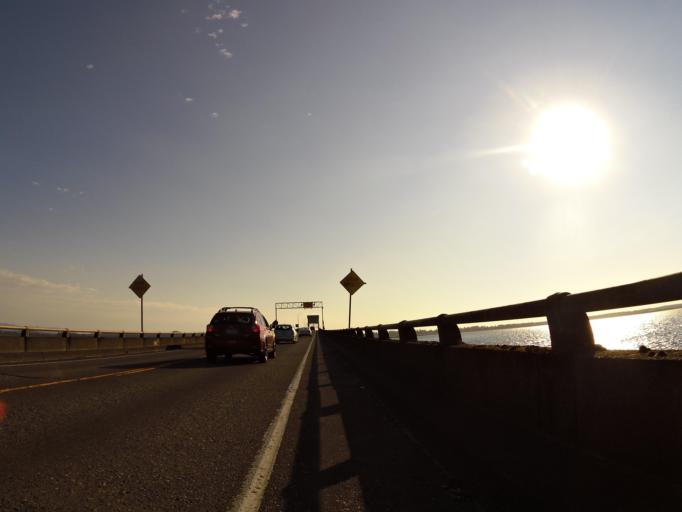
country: US
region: Oregon
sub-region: Clatsop County
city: Astoria
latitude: 46.1798
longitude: -123.8641
